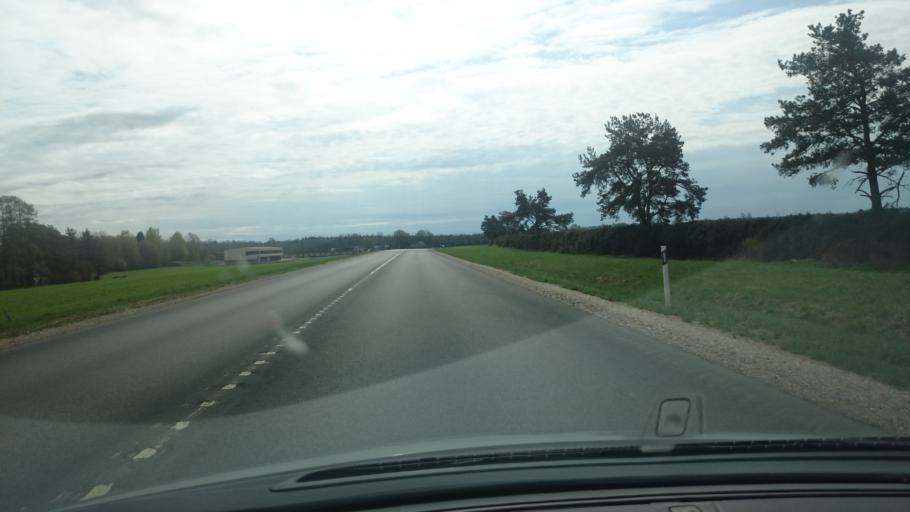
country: EE
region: Laeaene-Virumaa
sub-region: Someru vald
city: Someru
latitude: 59.3743
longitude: 26.4243
